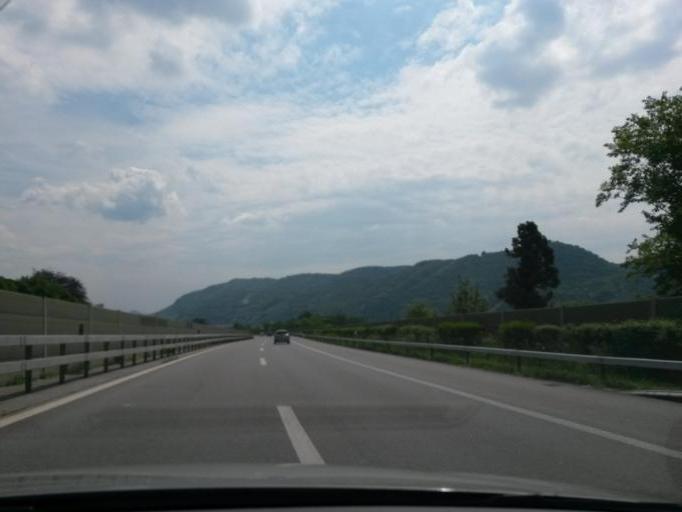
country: CH
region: Ticino
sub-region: Mendrisio District
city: Balerna
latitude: 45.8462
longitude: 8.9949
